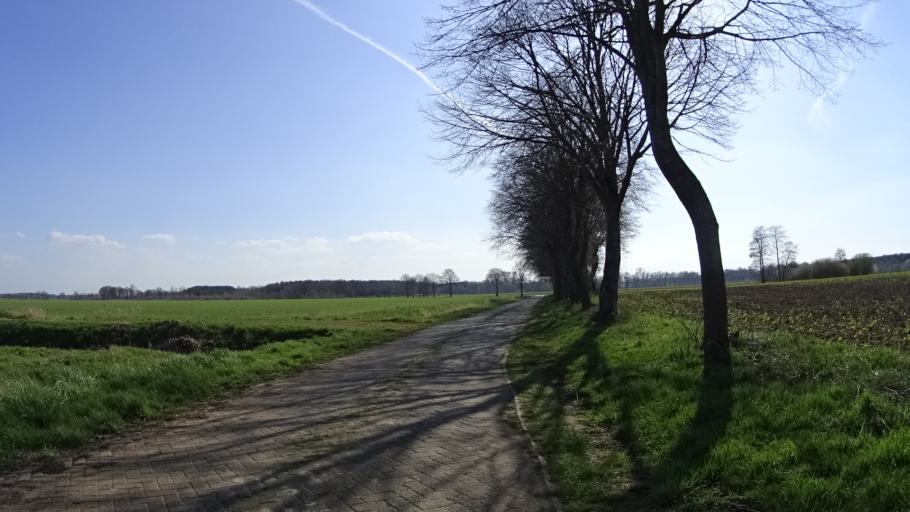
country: DE
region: Lower Saxony
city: Lehe
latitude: 52.9989
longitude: 7.3240
